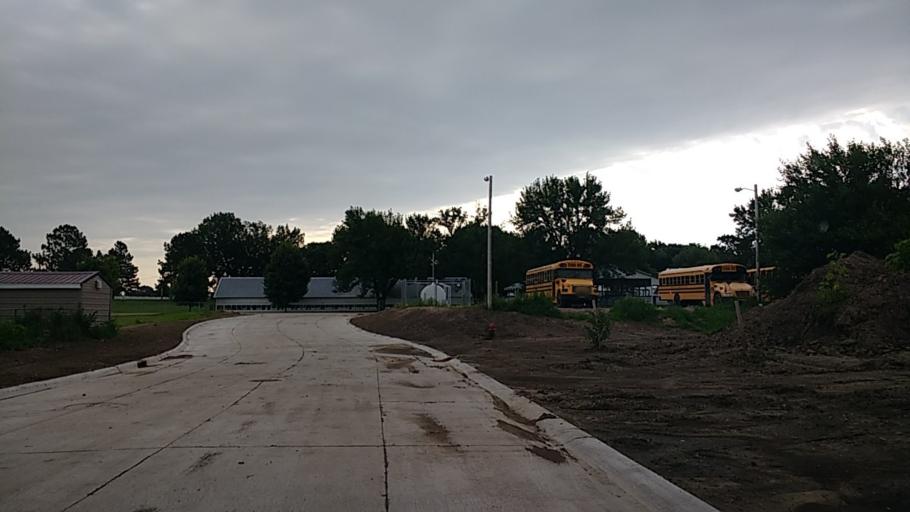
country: US
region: Iowa
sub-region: Woodbury County
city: Moville
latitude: 42.4875
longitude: -96.0664
